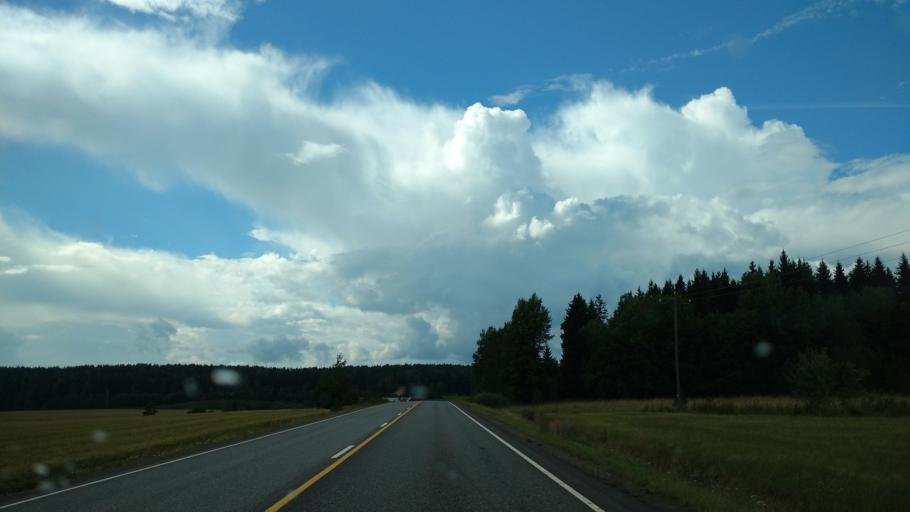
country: FI
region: Varsinais-Suomi
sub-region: Turku
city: Sauvo
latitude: 60.4083
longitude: 22.7980
